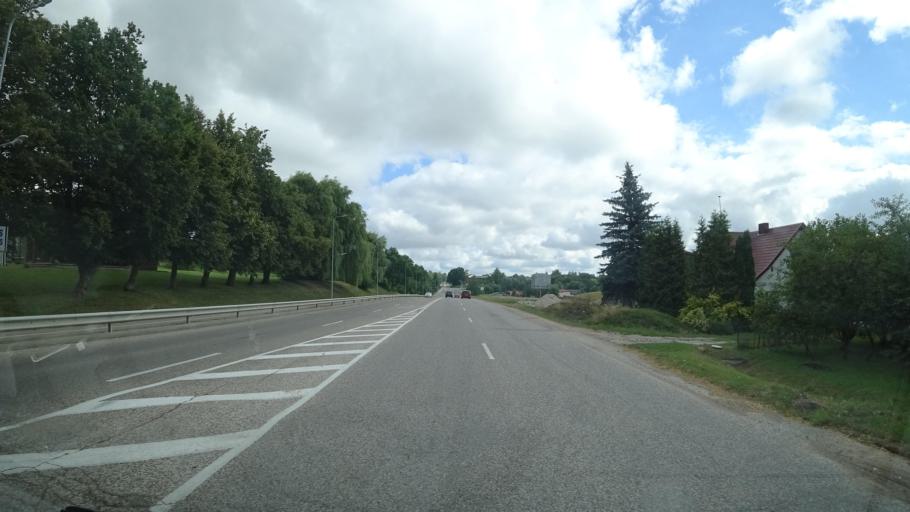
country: LT
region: Marijampoles apskritis
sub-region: Marijampole Municipality
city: Marijampole
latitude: 54.5341
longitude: 23.3354
